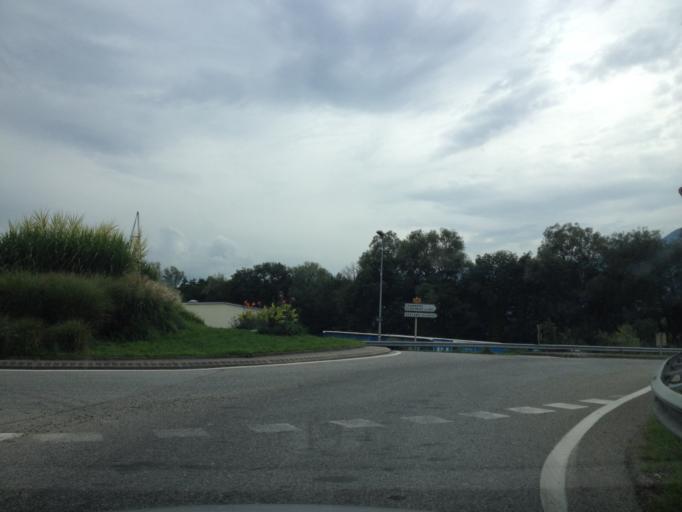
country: FR
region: Rhone-Alpes
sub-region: Departement de la Savoie
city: Voglans
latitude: 45.6253
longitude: 5.8932
